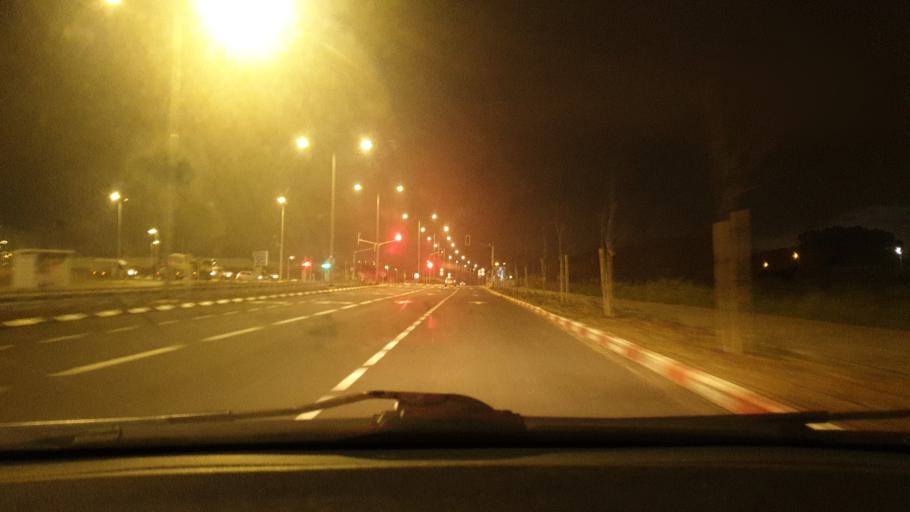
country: IL
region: Central District
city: Ramla
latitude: 31.9306
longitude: 34.8459
